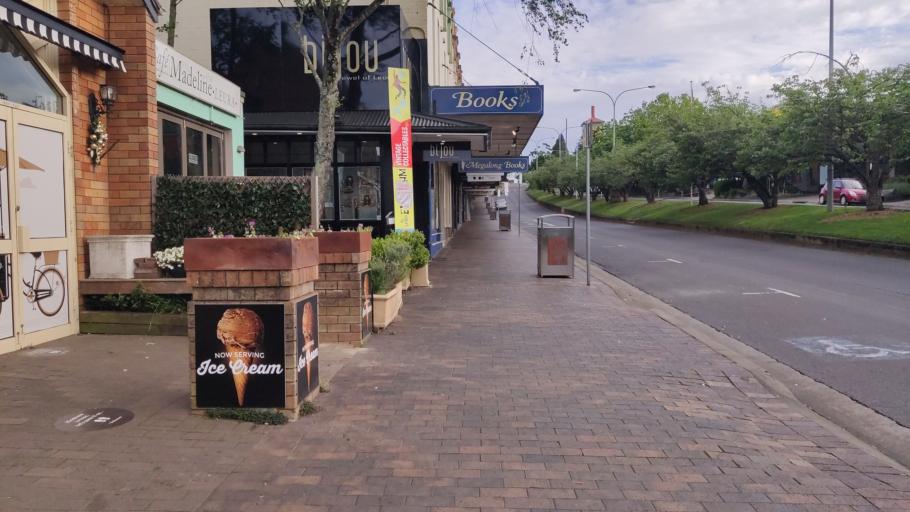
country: AU
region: New South Wales
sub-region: Blue Mountains Municipality
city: Leura
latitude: -33.7138
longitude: 150.3308
